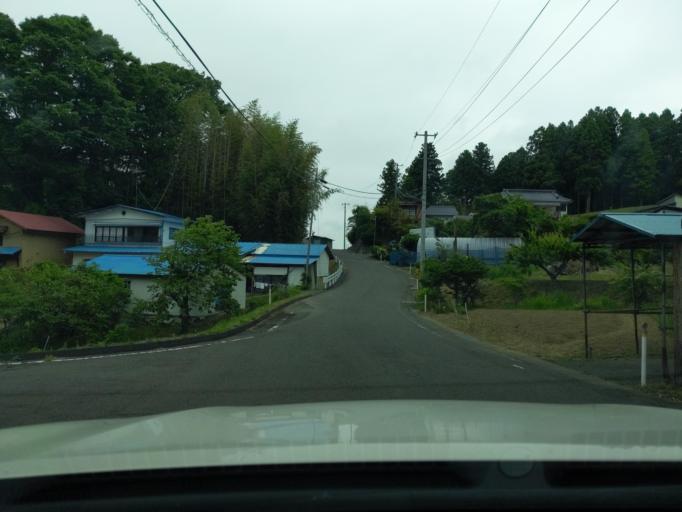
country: JP
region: Fukushima
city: Miharu
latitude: 37.4144
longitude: 140.4420
